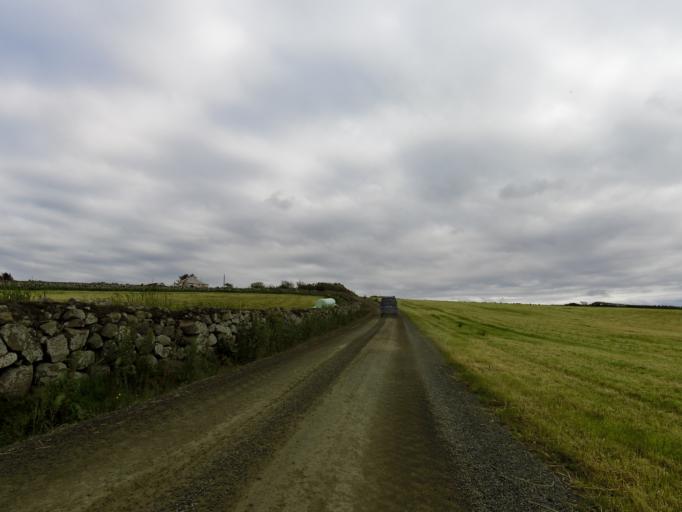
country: NO
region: Vest-Agder
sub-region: Farsund
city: Vestbygd
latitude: 58.1371
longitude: 6.6060
